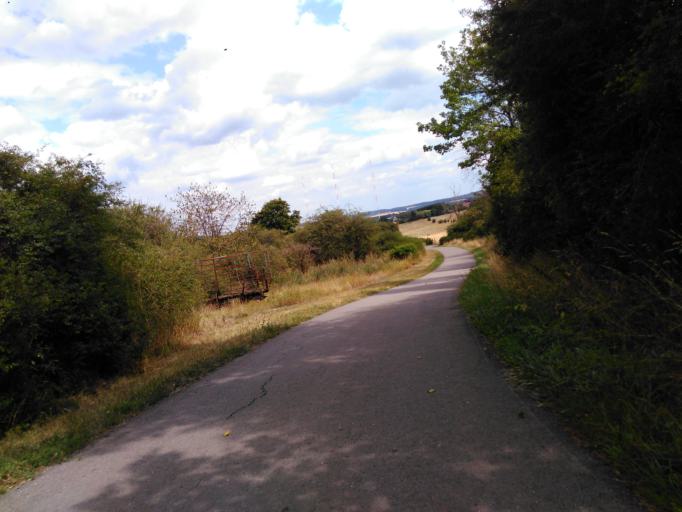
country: LU
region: Grevenmacher
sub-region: Canton de Grevenmacher
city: Junglinster
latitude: 49.7254
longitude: 6.2864
